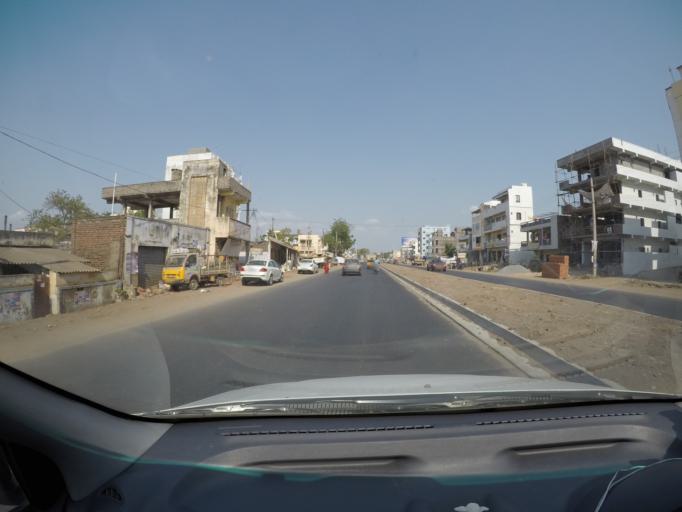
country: IN
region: Andhra Pradesh
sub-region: Krishna
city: Yanamalakuduru
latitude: 16.4772
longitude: 80.7043
